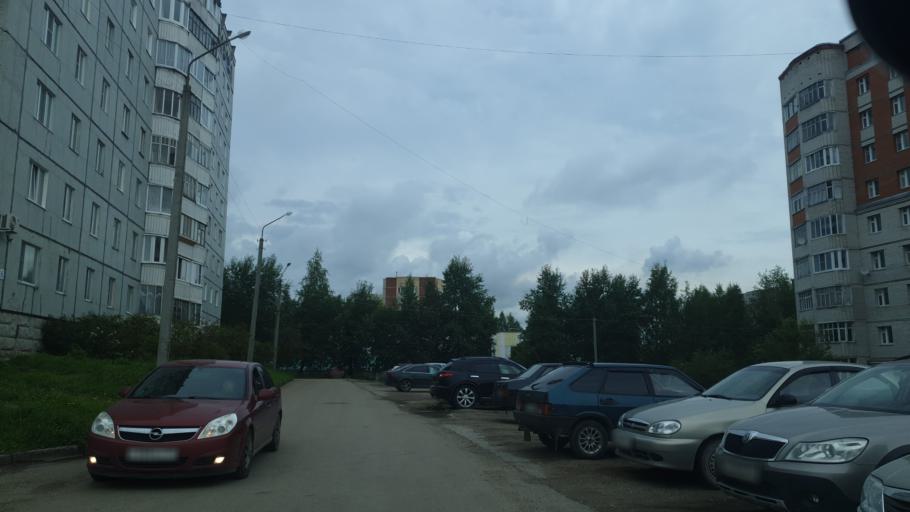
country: RU
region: Komi Republic
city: Ezhva
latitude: 61.7829
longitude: 50.7568
